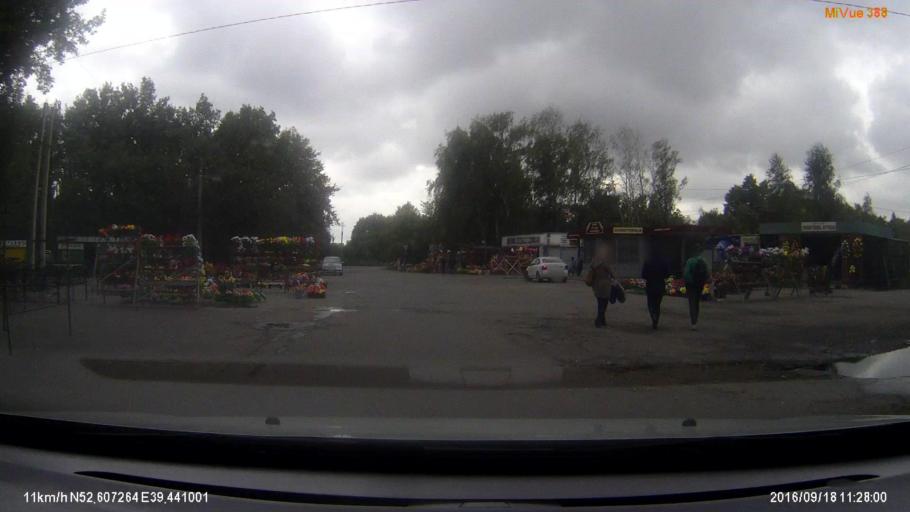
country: RU
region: Lipetsk
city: Syrskoye
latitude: 52.6073
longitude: 39.4407
